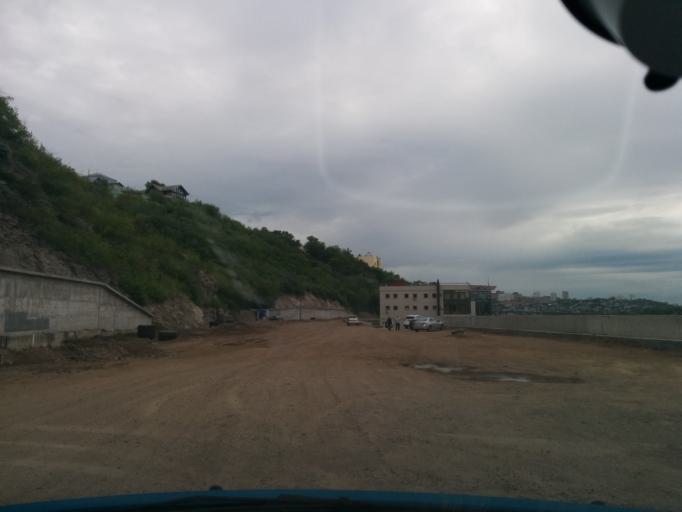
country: RU
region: Bashkortostan
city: Ufa
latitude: 54.7148
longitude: 55.9327
